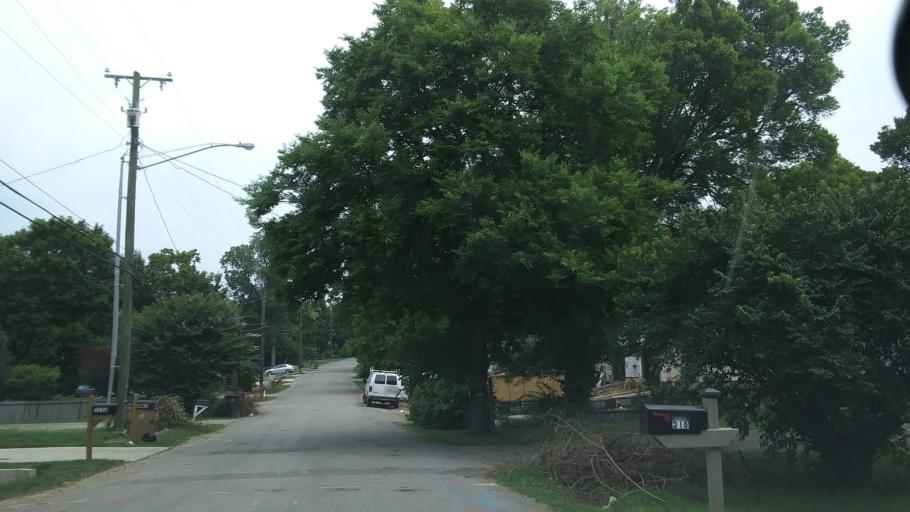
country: US
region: Tennessee
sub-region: Davidson County
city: Belle Meade
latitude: 36.1521
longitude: -86.8679
